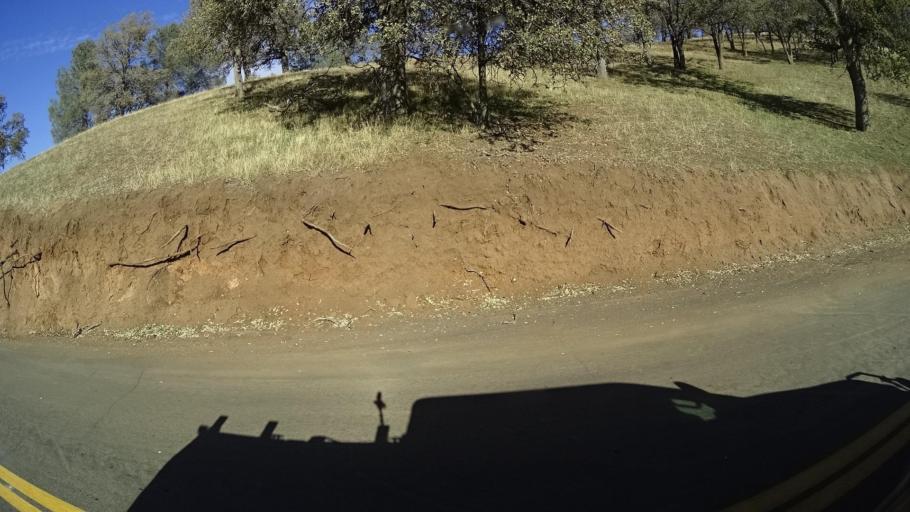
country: US
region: California
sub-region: Kern County
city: Bear Valley Springs
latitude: 35.3644
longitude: -118.5535
